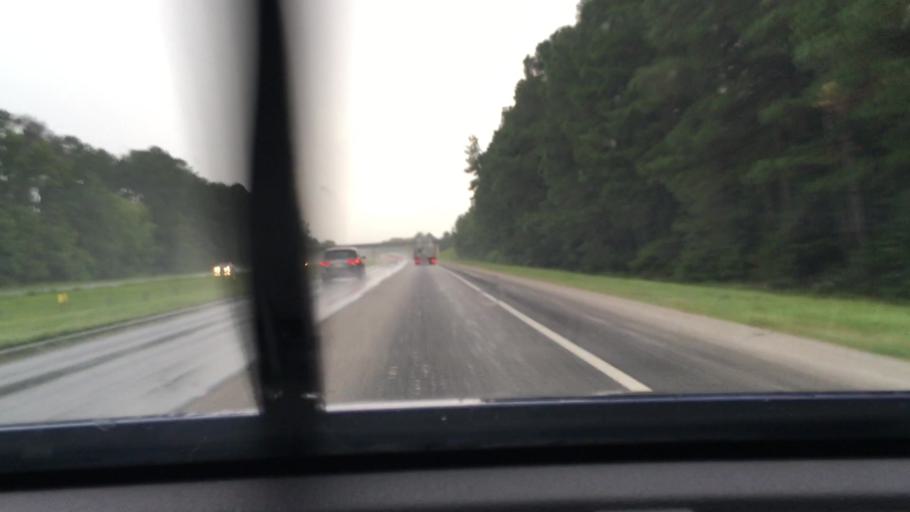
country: US
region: South Carolina
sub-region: Lee County
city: Bishopville
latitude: 34.1946
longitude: -80.1359
